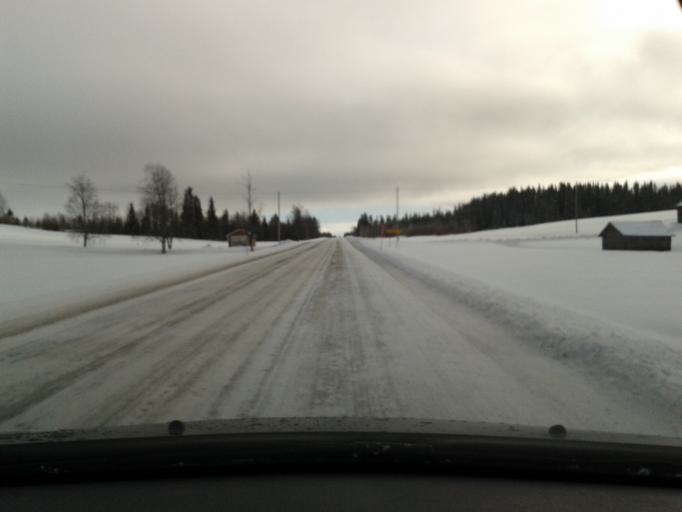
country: SE
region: Vaesterbotten
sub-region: Vilhelmina Kommun
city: Sjoberg
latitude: 64.7898
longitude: 16.0966
